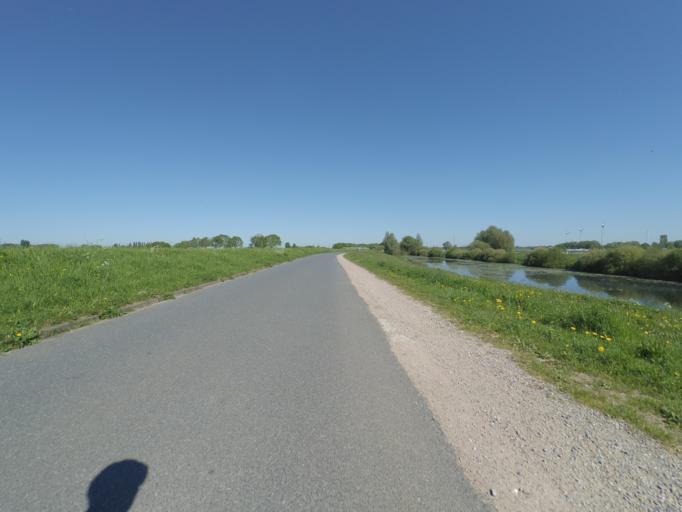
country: NL
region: Gelderland
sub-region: Gemeente Zutphen
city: Zutphen
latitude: 52.1469
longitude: 6.1827
